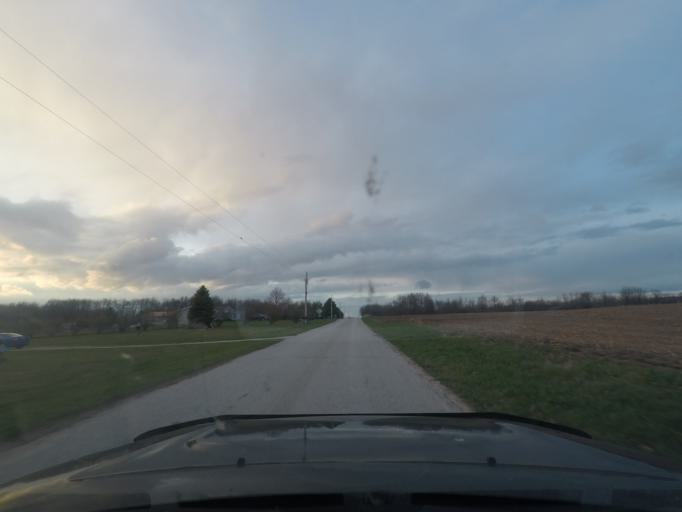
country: US
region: Indiana
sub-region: LaPorte County
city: Kingsford Heights
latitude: 41.4671
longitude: -86.6999
